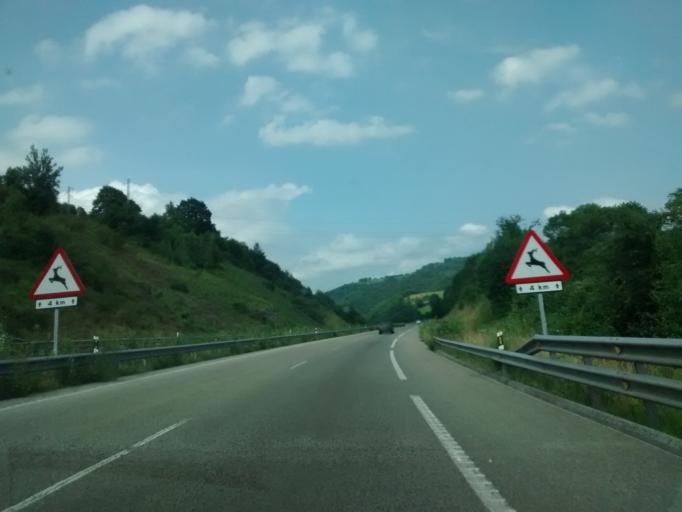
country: ES
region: Asturias
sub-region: Province of Asturias
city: Mieres
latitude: 43.2969
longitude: -5.7554
